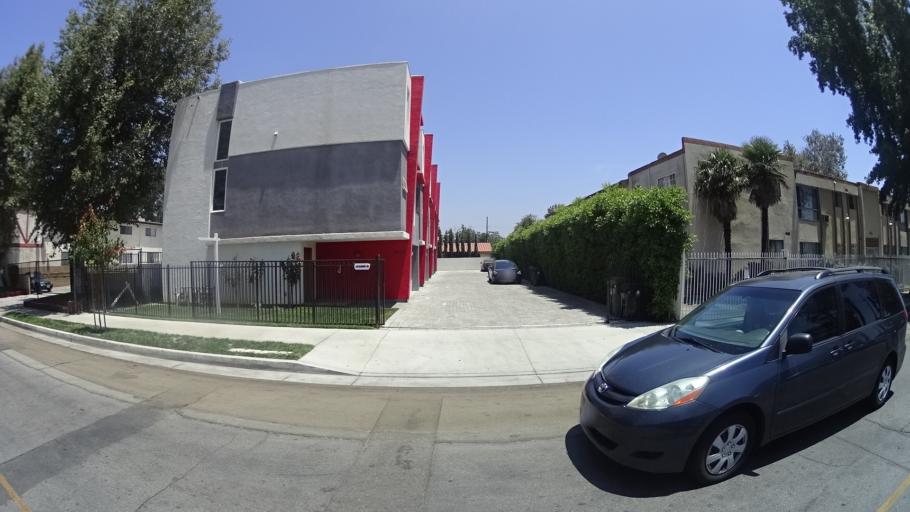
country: US
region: California
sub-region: Los Angeles County
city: Van Nuys
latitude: 34.1963
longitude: -118.4455
